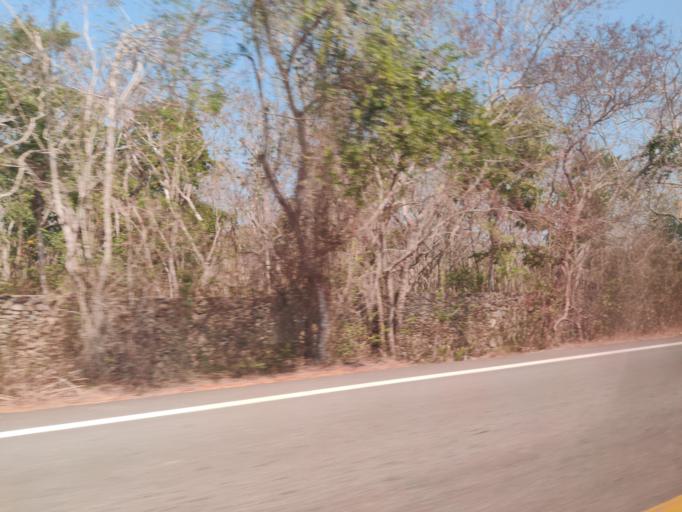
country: CO
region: Bolivar
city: Turbana
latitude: 10.1772
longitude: -75.6458
